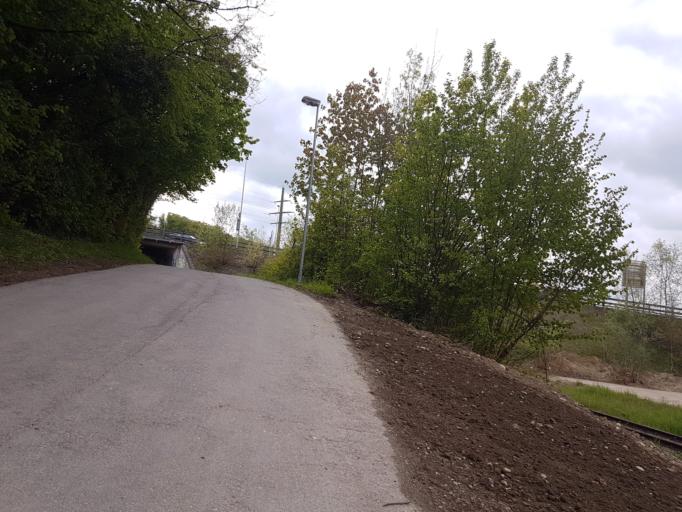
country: CH
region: Solothurn
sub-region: Bezirk Solothurn
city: Solothurn
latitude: 47.1978
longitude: 7.5322
